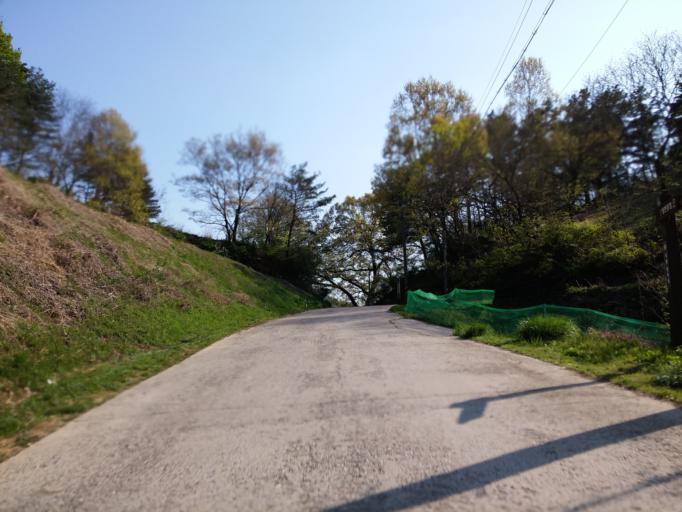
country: KR
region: Daejeon
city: Sintansin
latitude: 36.4214
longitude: 127.4823
